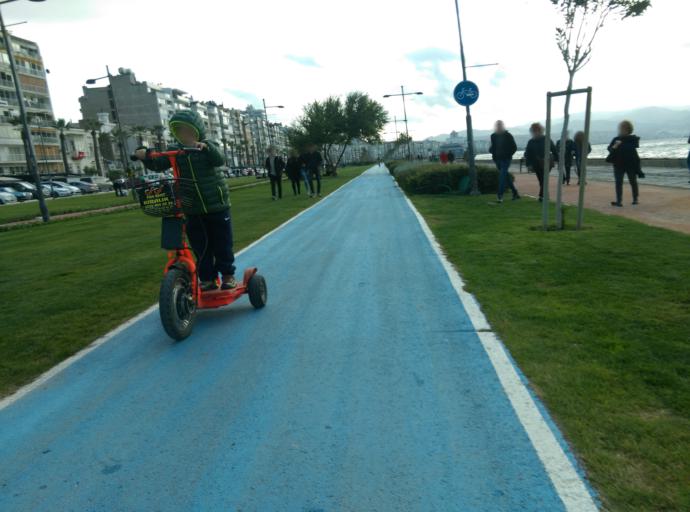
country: TR
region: Izmir
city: Izmir
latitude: 38.4416
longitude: 27.1423
